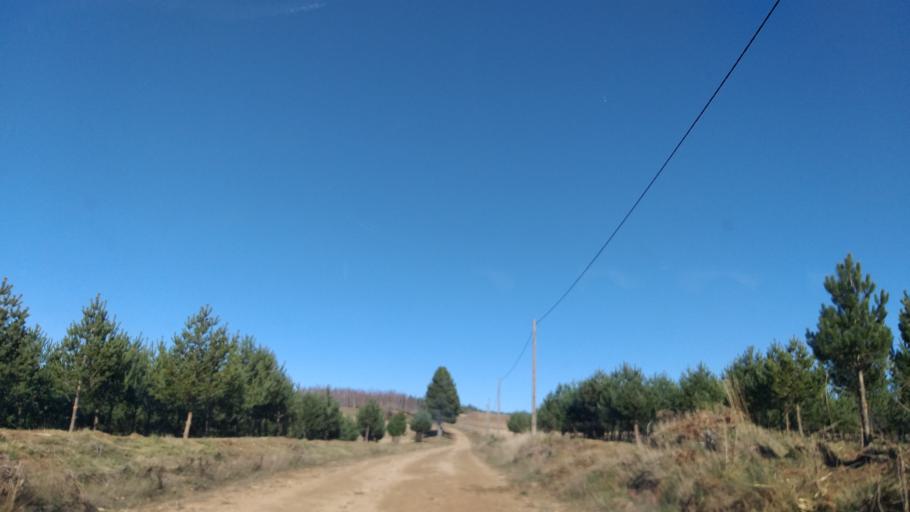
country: PT
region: Guarda
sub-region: Manteigas
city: Manteigas
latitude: 40.5127
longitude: -7.4571
